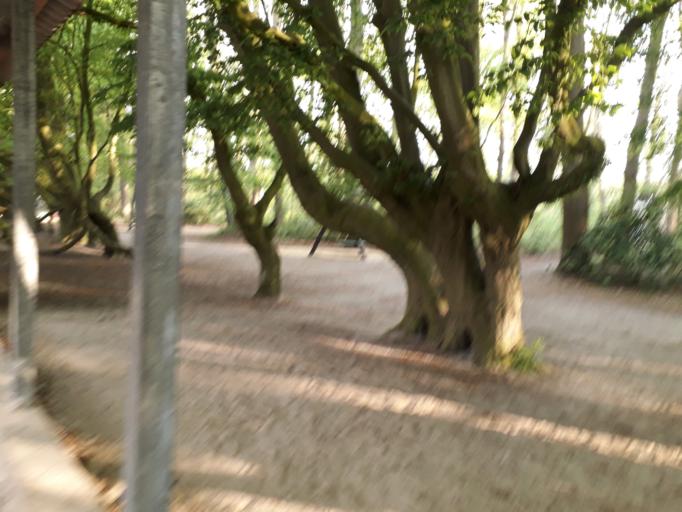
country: DE
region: Lower Saxony
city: Haren
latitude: 52.7961
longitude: 7.2016
